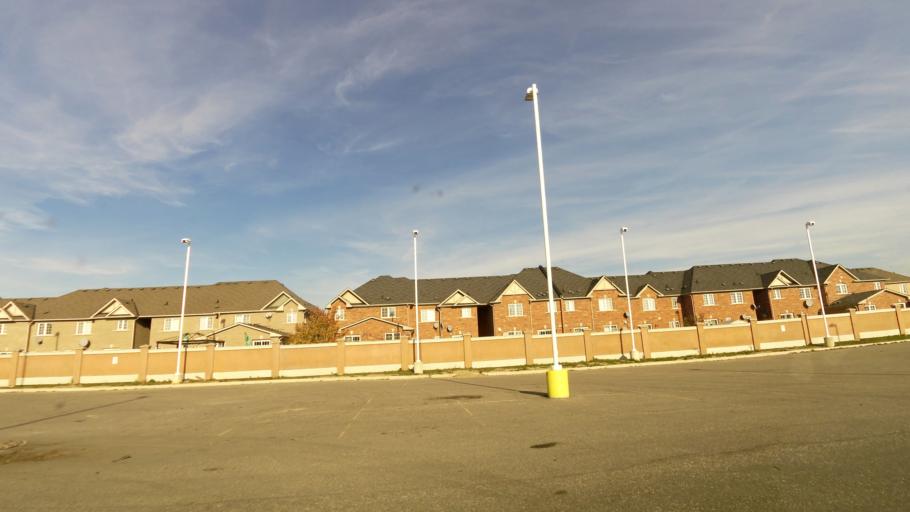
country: CA
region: Ontario
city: Brampton
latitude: 43.7702
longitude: -79.7539
